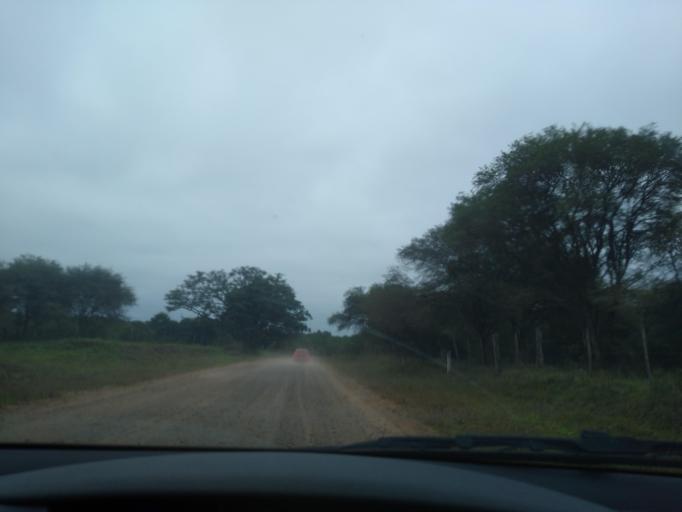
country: AR
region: Chaco
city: Colonia Benitez
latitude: -27.3409
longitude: -58.9690
